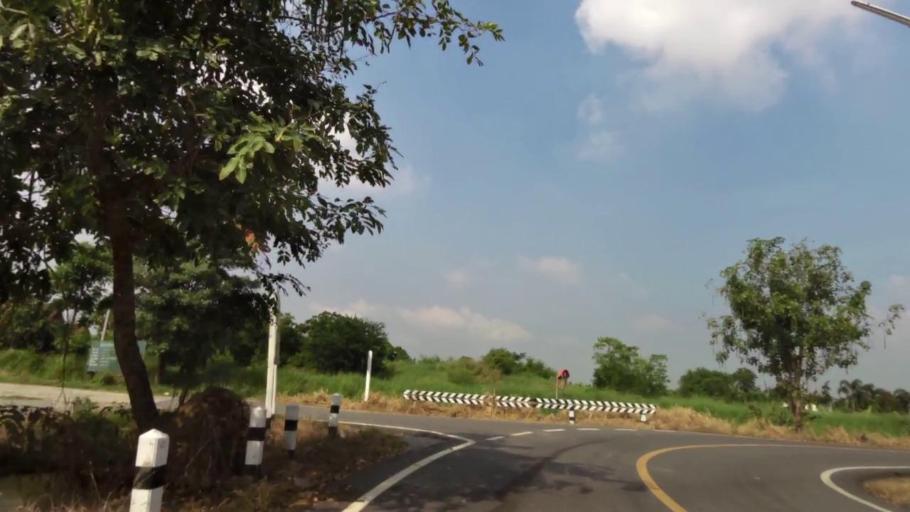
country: TH
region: Ang Thong
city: Pho Thong
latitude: 14.6135
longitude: 100.3946
